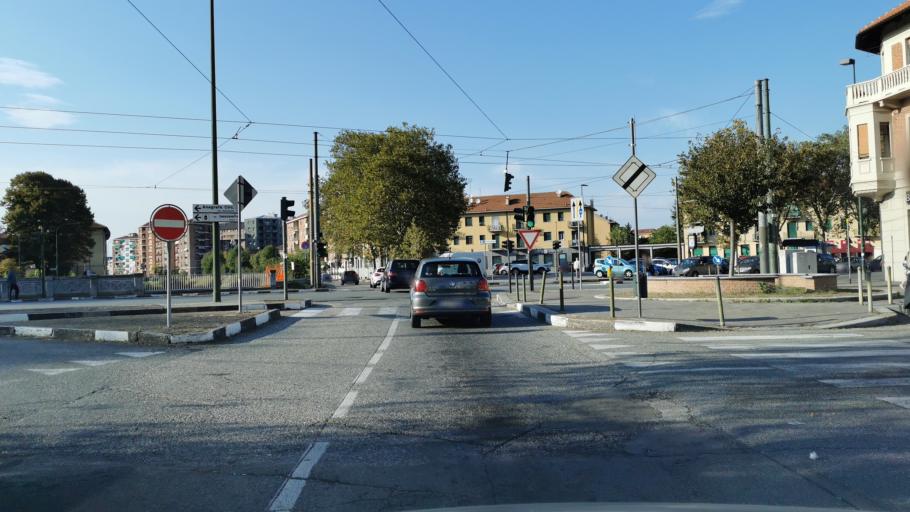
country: IT
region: Piedmont
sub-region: Provincia di Torino
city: Turin
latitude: 45.0904
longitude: 7.7124
